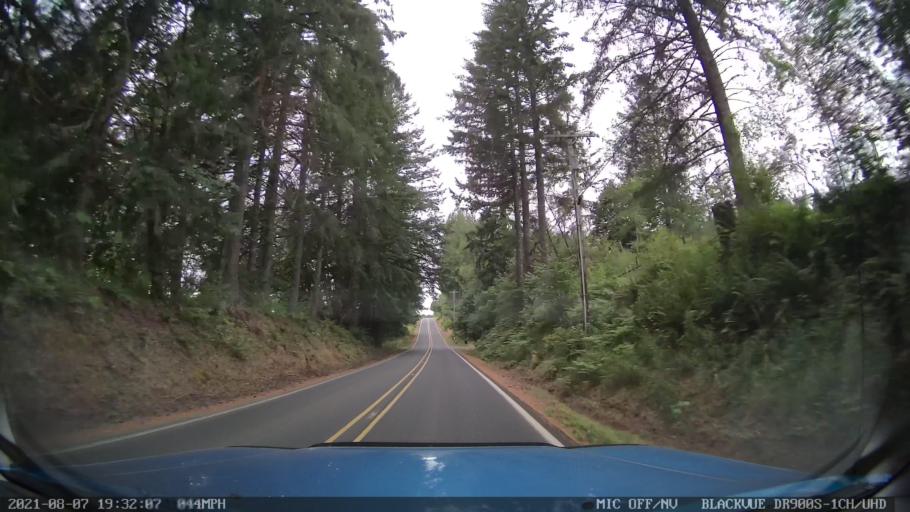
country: US
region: Oregon
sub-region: Linn County
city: Lyons
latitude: 44.8975
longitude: -122.6400
